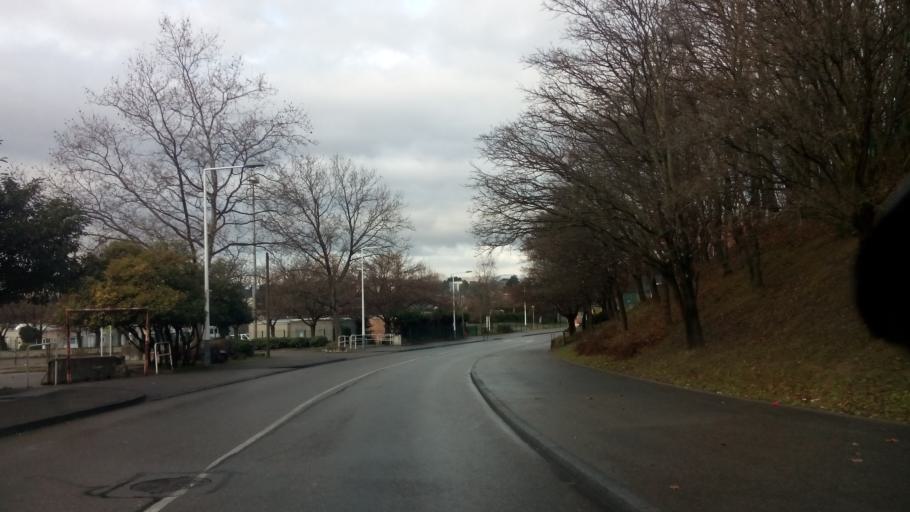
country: FR
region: Rhone-Alpes
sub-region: Departement du Rhone
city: Venissieux
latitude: 45.6902
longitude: 4.8684
